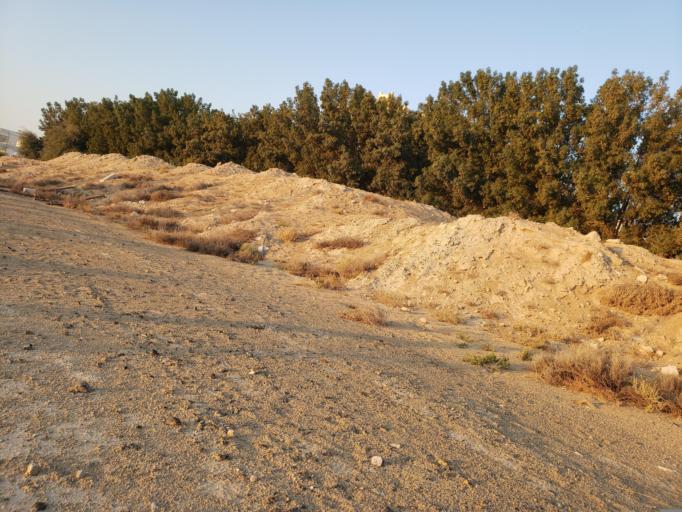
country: AE
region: Dubai
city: Dubai
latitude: 25.0029
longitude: 55.2460
